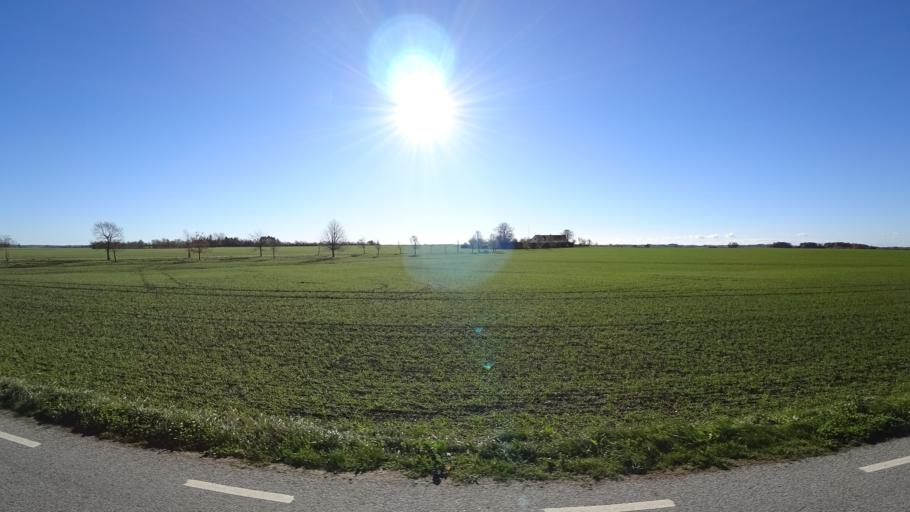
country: SE
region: Skane
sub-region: Svedala Kommun
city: Klagerup
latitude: 55.6166
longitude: 13.2927
